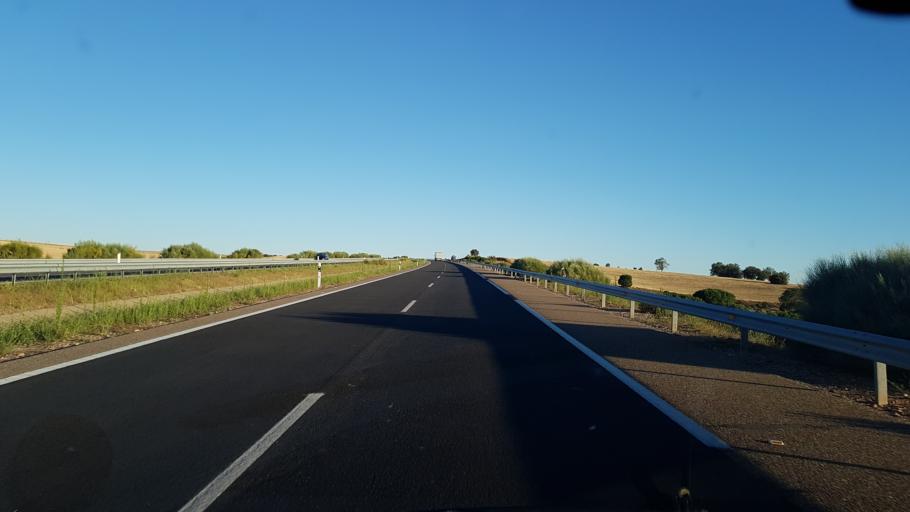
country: ES
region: Castille and Leon
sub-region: Provincia de Zamora
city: Matilla la Seca
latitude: 41.5629
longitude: -5.4784
